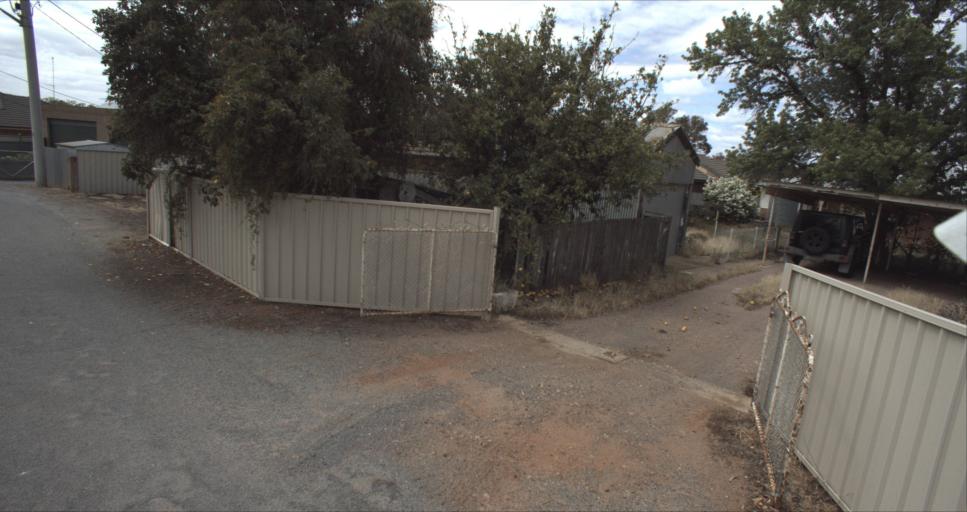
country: AU
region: New South Wales
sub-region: Leeton
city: Leeton
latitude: -34.5553
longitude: 146.4072
